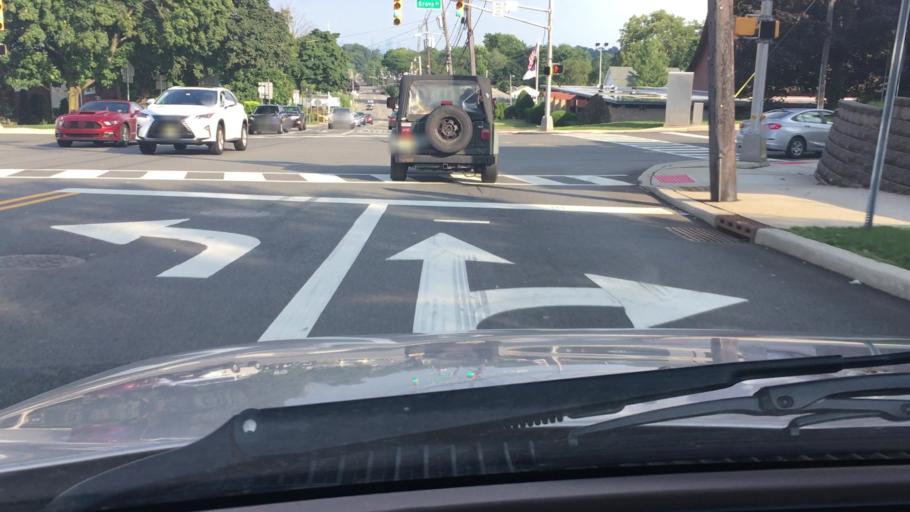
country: US
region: New Jersey
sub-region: Passaic County
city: Clifton
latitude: 40.8727
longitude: -74.1742
